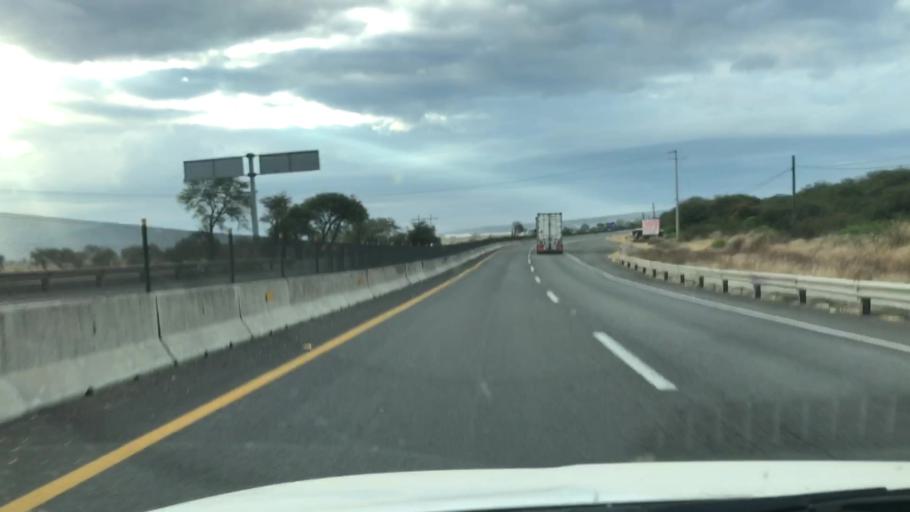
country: MX
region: Guanajuato
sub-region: Penjamo
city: Mezquite de Luna
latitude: 20.3847
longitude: -101.9048
